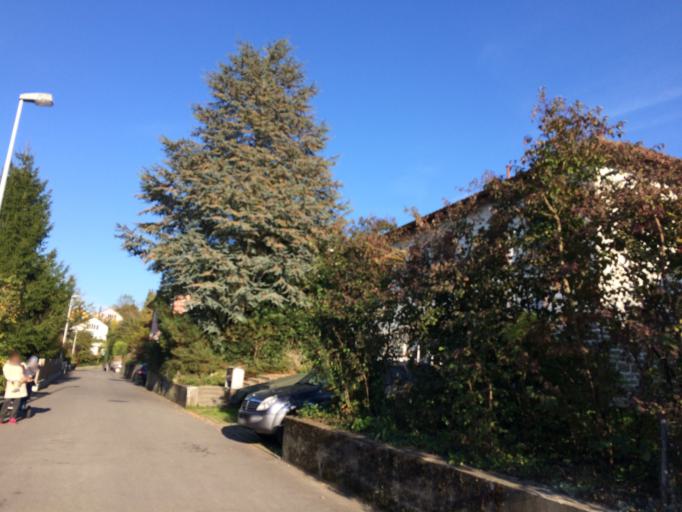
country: CH
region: Bern
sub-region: Bern-Mittelland District
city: Koniz
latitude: 46.9256
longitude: 7.4215
